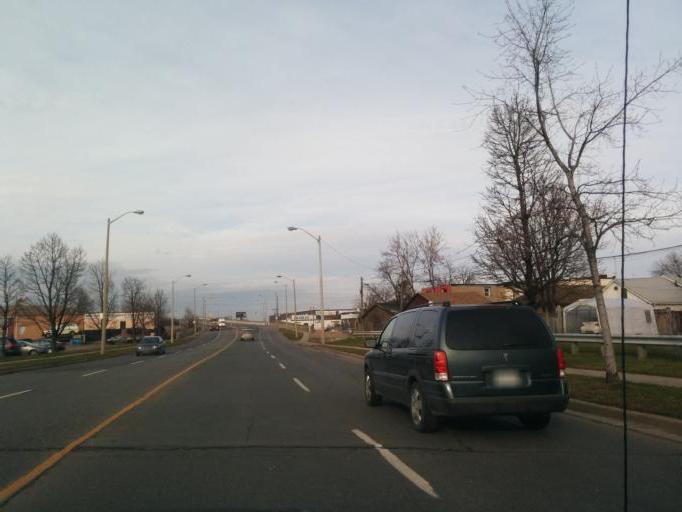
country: CA
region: Ontario
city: Etobicoke
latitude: 43.6044
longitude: -79.5066
